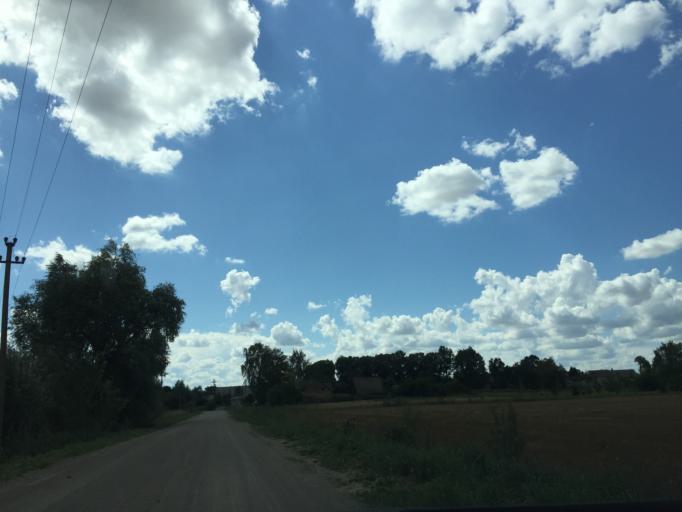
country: LV
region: Rundales
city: Pilsrundale
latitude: 56.2783
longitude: 23.9960
